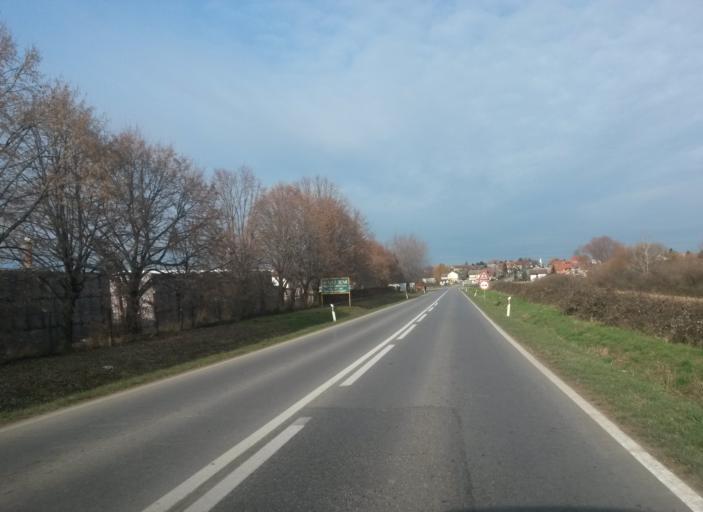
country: HR
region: Osjecko-Baranjska
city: Viskovci
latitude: 45.3410
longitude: 18.4211
